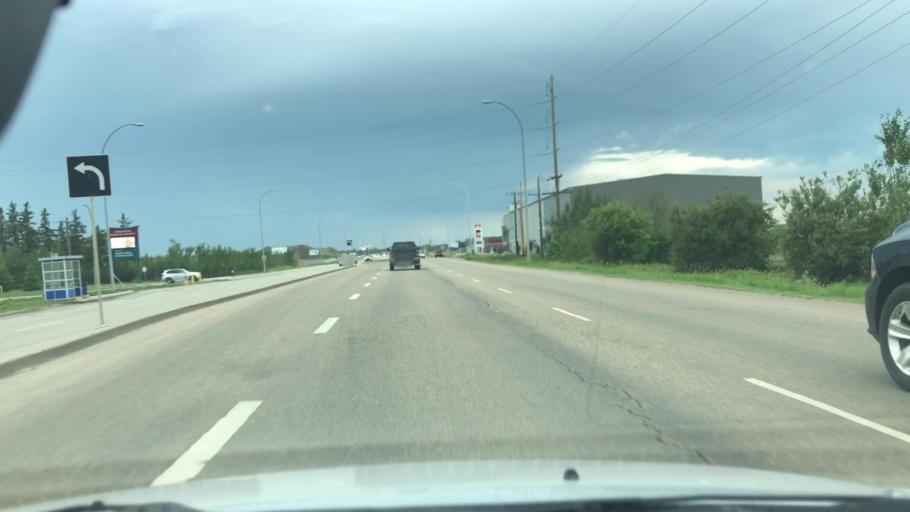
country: CA
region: Alberta
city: St. Albert
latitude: 53.5994
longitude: -113.6011
